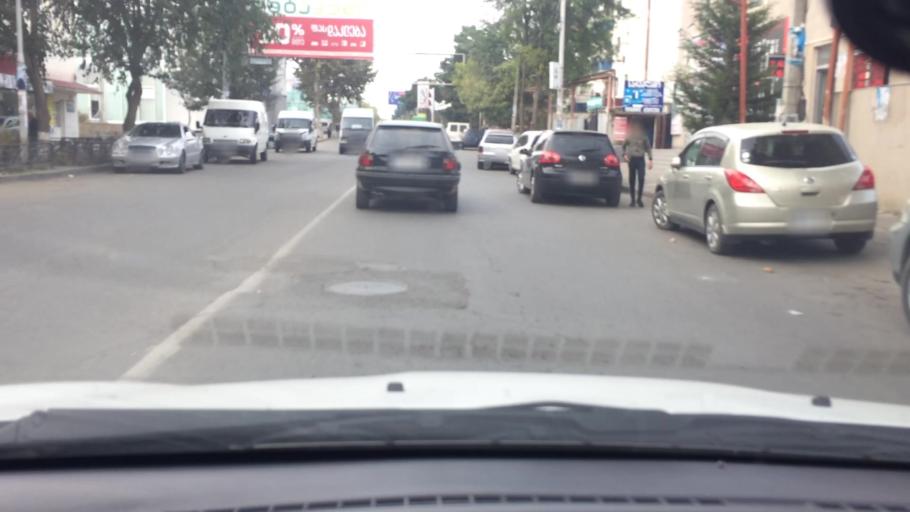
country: GE
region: Kvemo Kartli
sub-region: Marneuli
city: Marneuli
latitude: 41.4865
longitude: 44.8002
